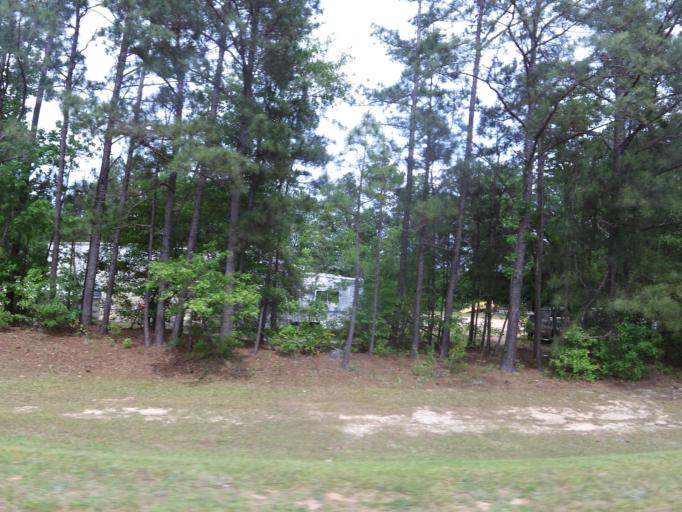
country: US
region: Georgia
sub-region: McDuffie County
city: Thomson
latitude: 33.3587
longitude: -82.4639
